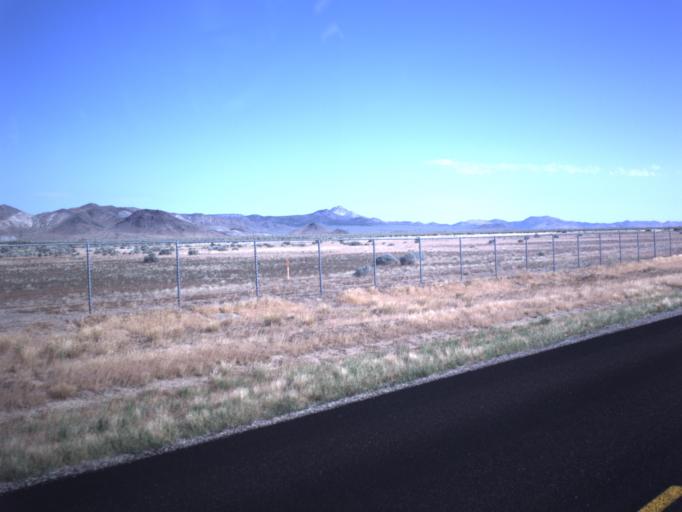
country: US
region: Utah
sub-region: Beaver County
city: Milford
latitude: 38.4238
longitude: -113.0098
